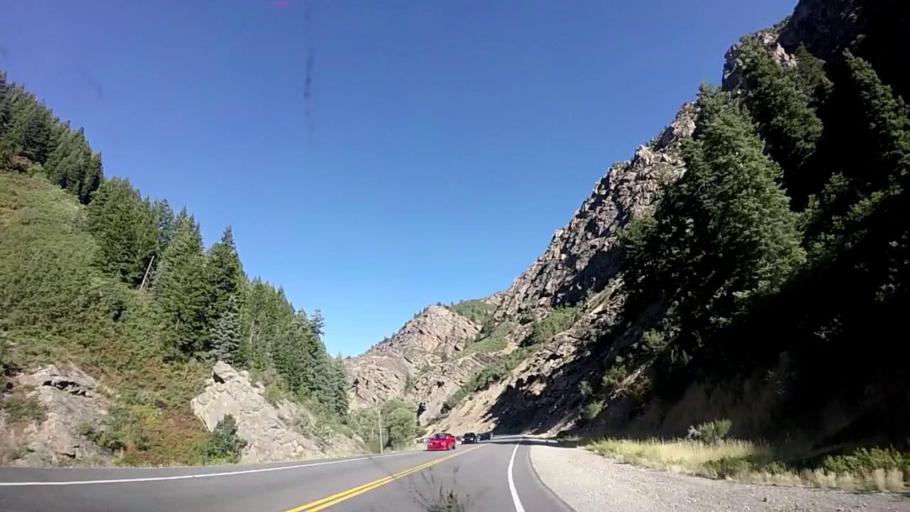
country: US
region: Utah
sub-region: Salt Lake County
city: Mount Olympus
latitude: 40.6331
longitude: -111.7063
